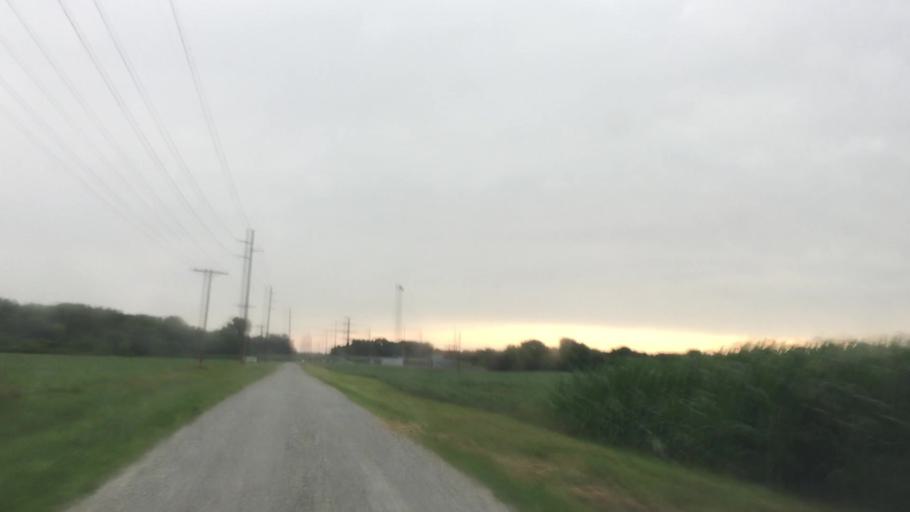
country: US
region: Iowa
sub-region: Lee County
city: Fort Madison
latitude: 40.6029
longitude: -91.2676
